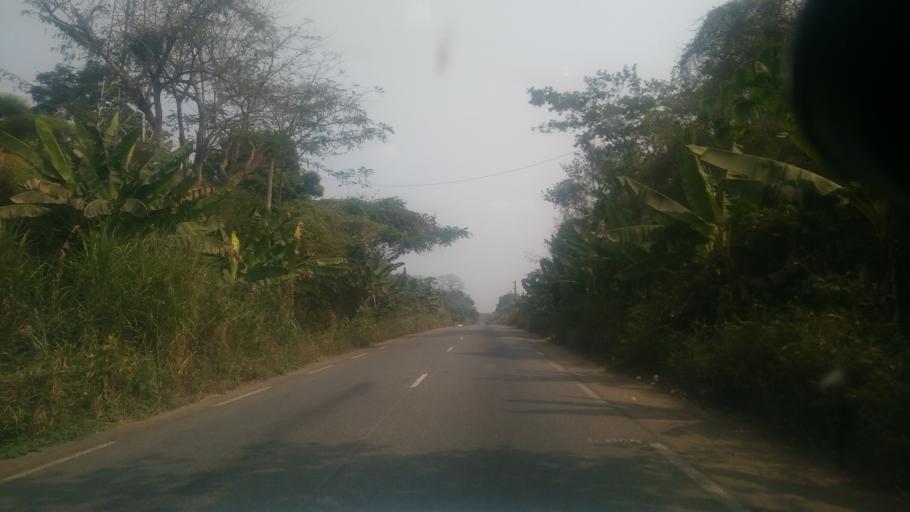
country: CM
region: Centre
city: Ombesa
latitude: 4.6550
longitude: 11.2509
